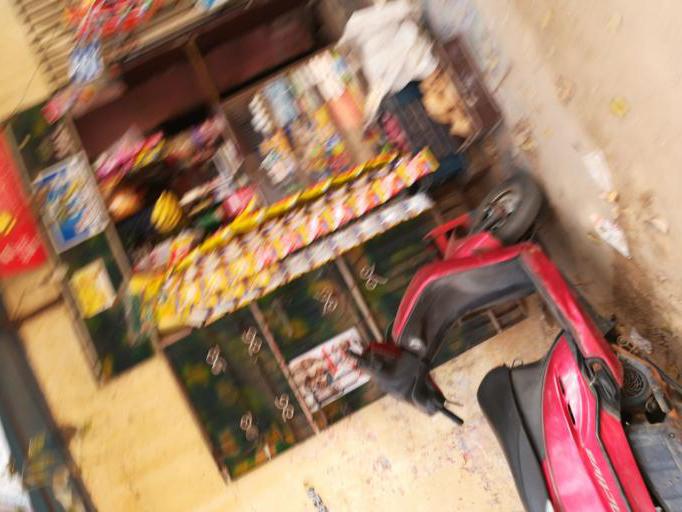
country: IN
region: Andhra Pradesh
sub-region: Nellore
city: Nellore
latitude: 14.4436
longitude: 79.9843
